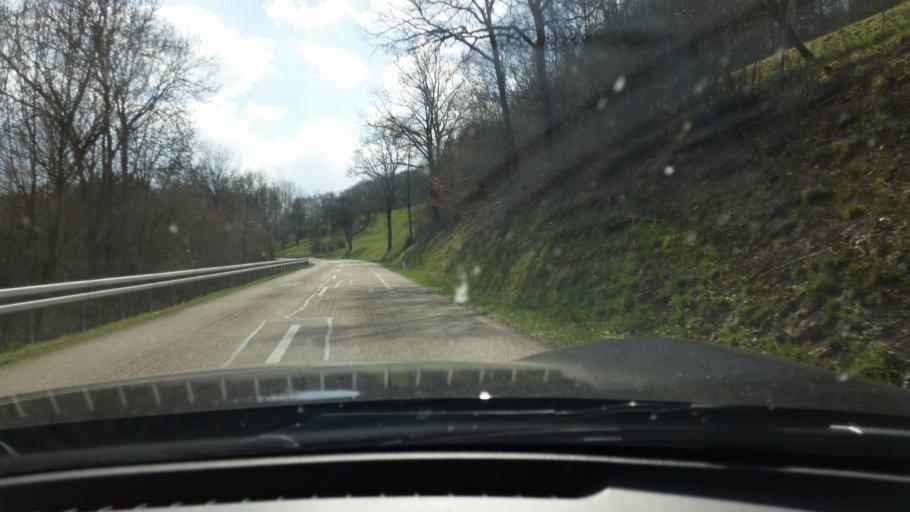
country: DE
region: Baden-Wuerttemberg
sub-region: Regierungsbezirk Stuttgart
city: Langenburg
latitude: 49.2668
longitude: 9.8284
